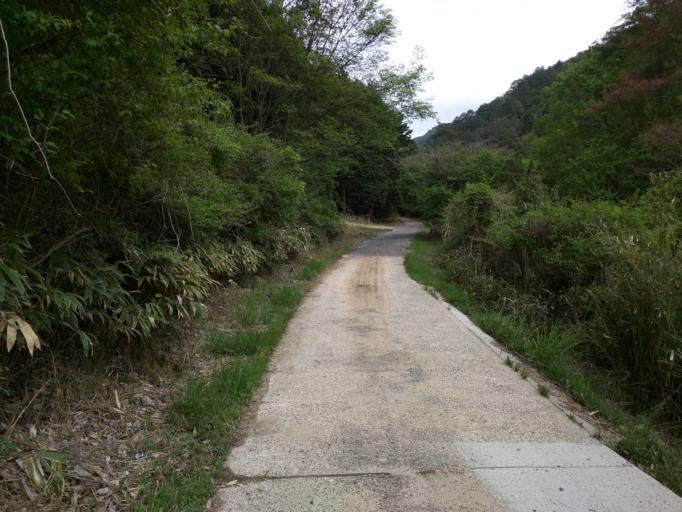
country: JP
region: Mie
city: Ueno-ebisumachi
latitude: 34.8254
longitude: 135.9971
